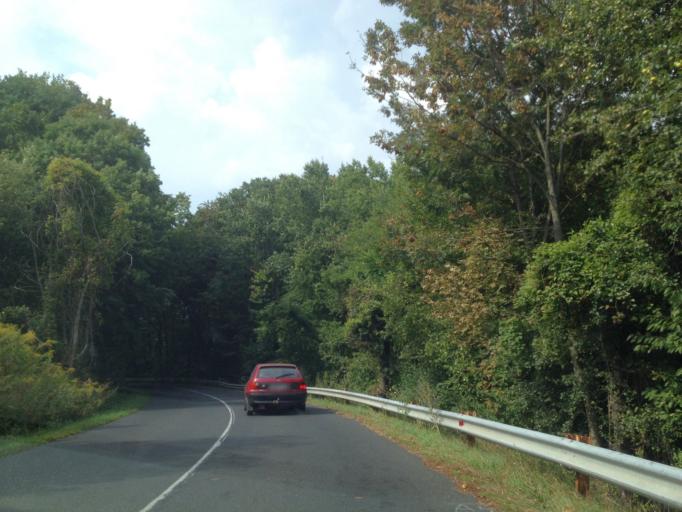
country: HU
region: Komarom-Esztergom
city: Kesztolc
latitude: 47.7306
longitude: 18.8365
